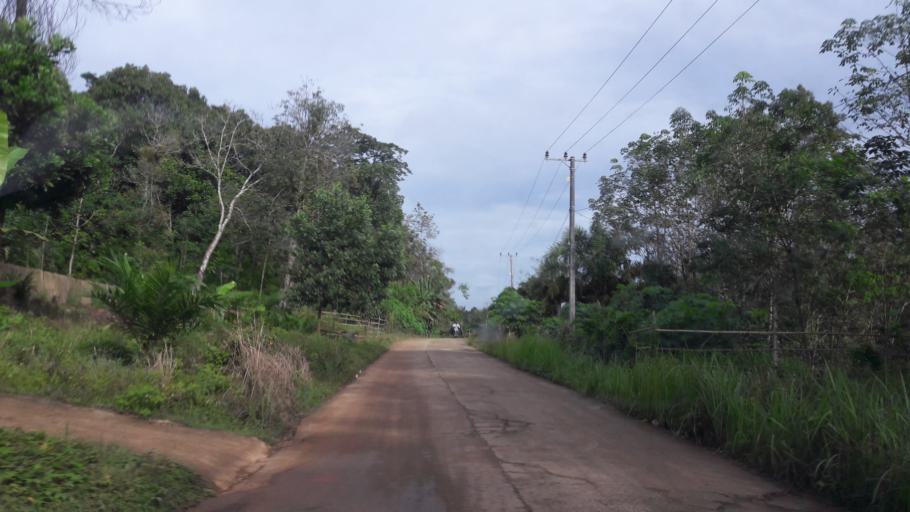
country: ID
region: South Sumatra
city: Gunungmegang Dalam
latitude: -3.2821
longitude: 103.7559
